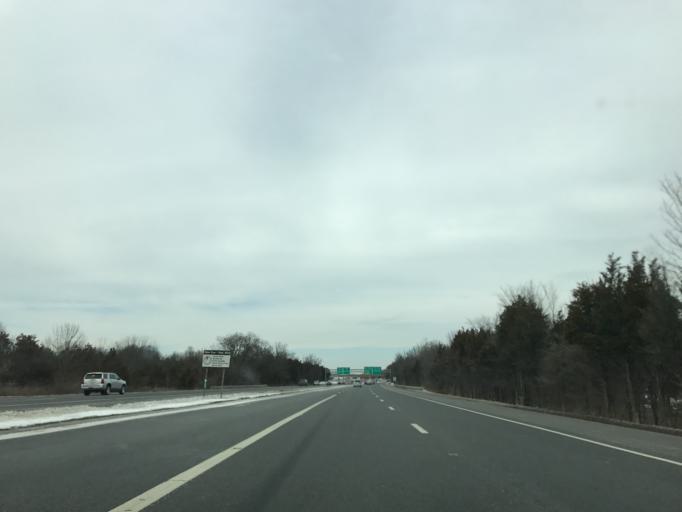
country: US
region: New Jersey
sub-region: Somerset County
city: Green Knoll
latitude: 40.6018
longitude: -74.6263
